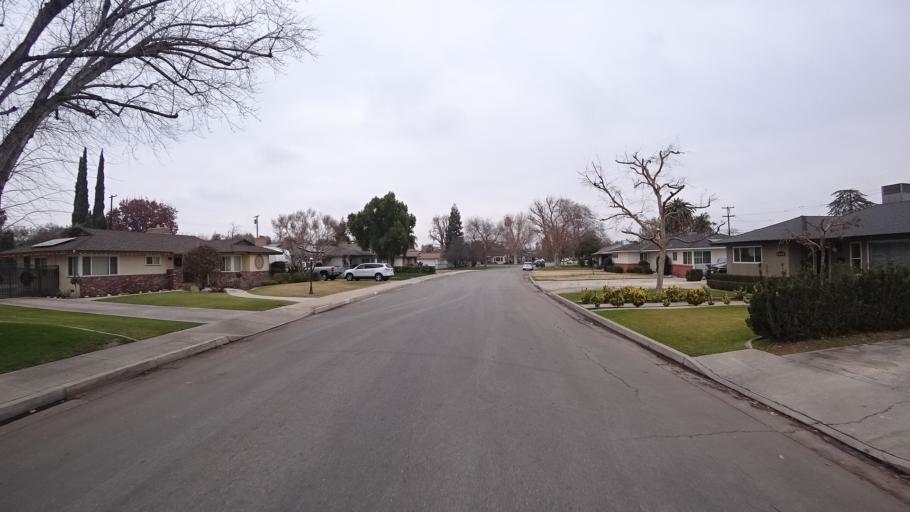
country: US
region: California
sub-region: Kern County
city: Bakersfield
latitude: 35.3828
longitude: -119.0304
